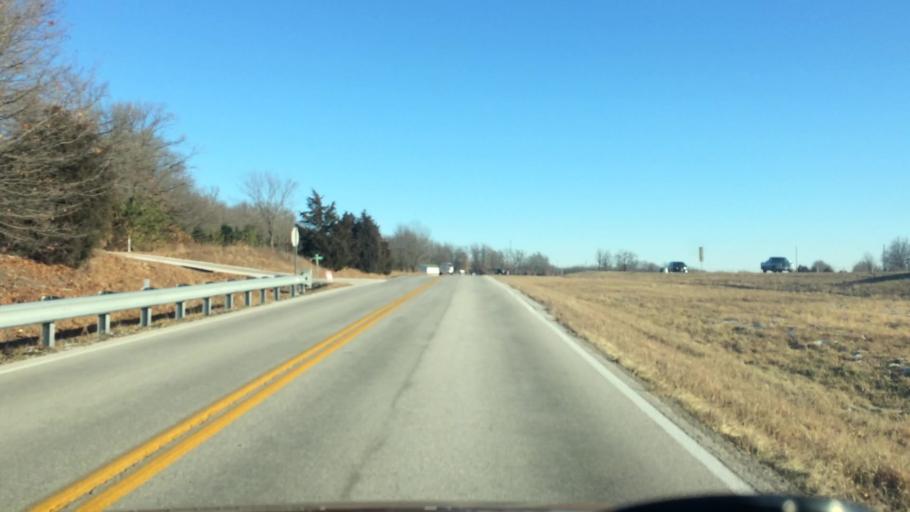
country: US
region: Missouri
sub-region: Greene County
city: Strafford
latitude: 37.2812
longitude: -93.0445
